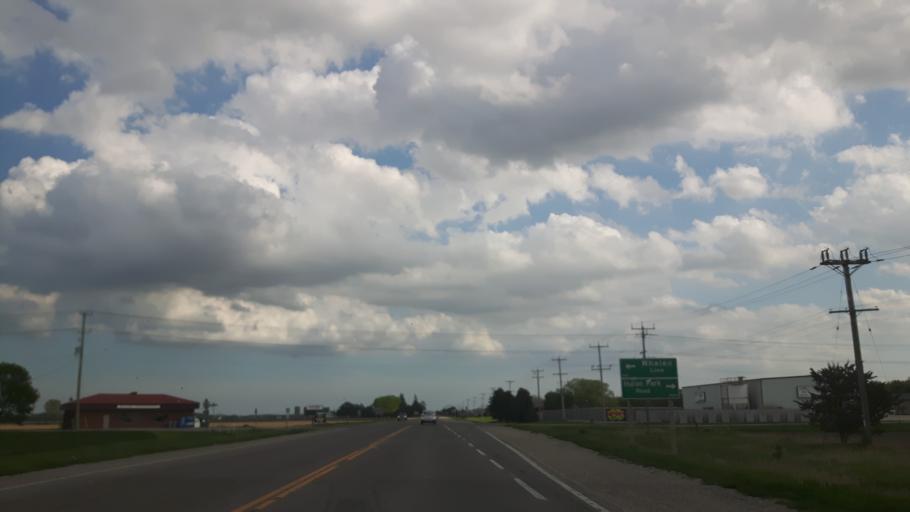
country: CA
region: Ontario
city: South Huron
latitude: 43.2898
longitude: -81.4691
